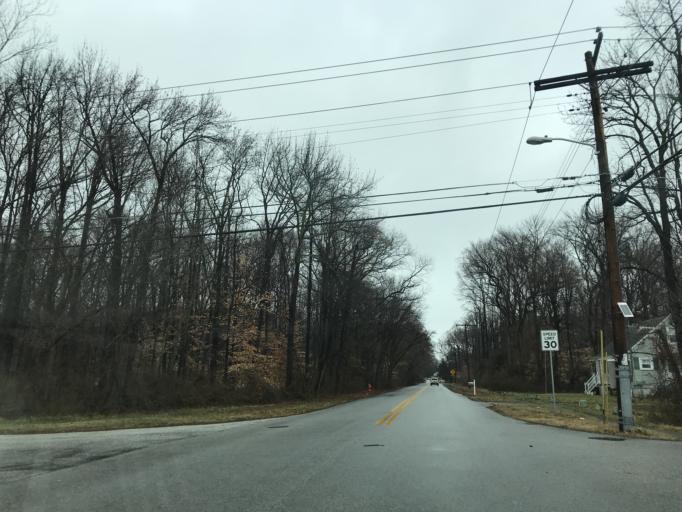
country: US
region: Maryland
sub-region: Baltimore County
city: Edgemere
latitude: 39.2294
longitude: -76.4435
